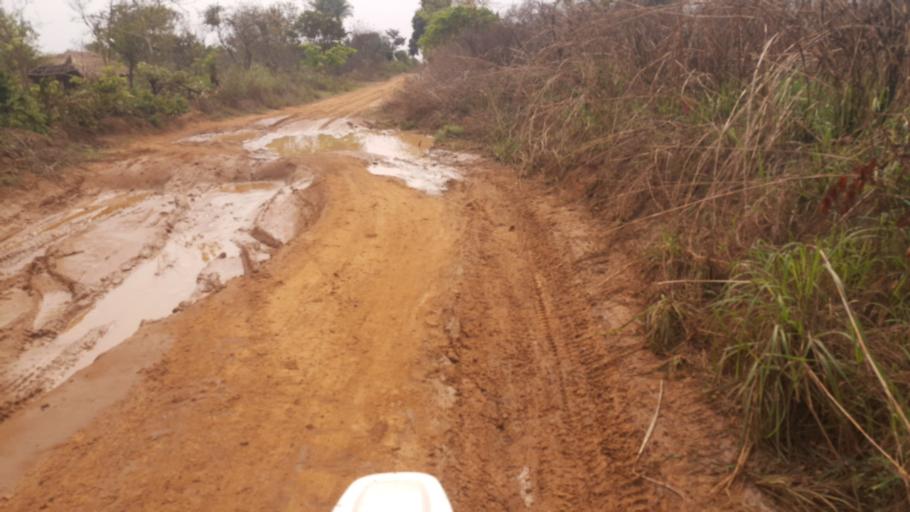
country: CD
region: Bandundu
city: Bandundu
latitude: -3.4575
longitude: 17.7358
